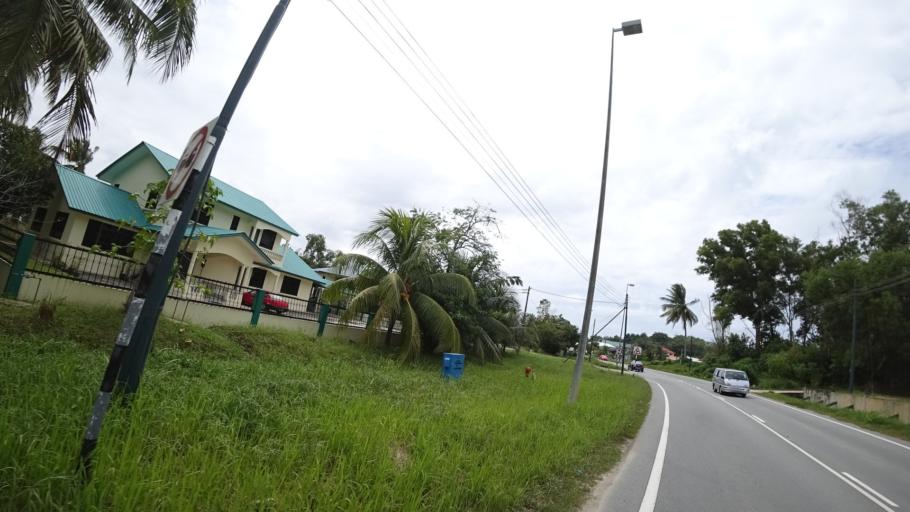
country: BN
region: Tutong
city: Tutong
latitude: 4.8044
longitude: 114.6680
